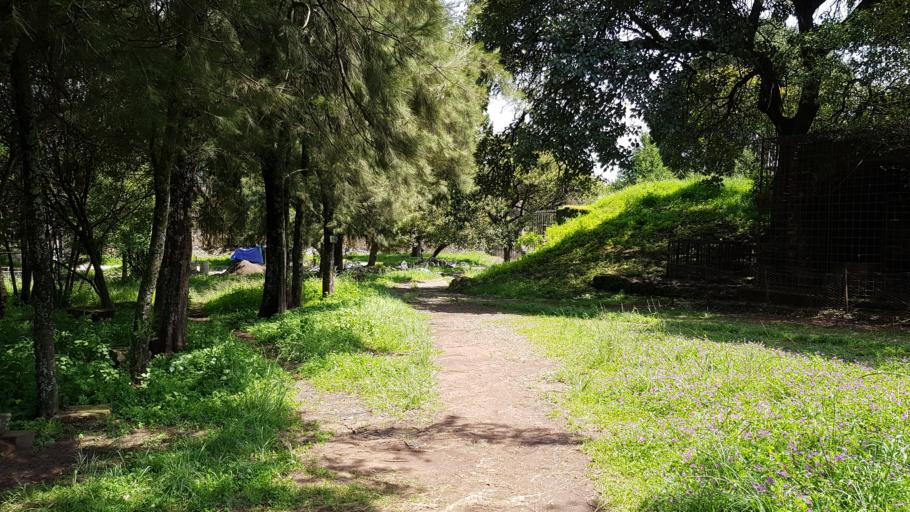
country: ET
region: Amhara
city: Gondar
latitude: 12.6084
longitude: 37.4696
